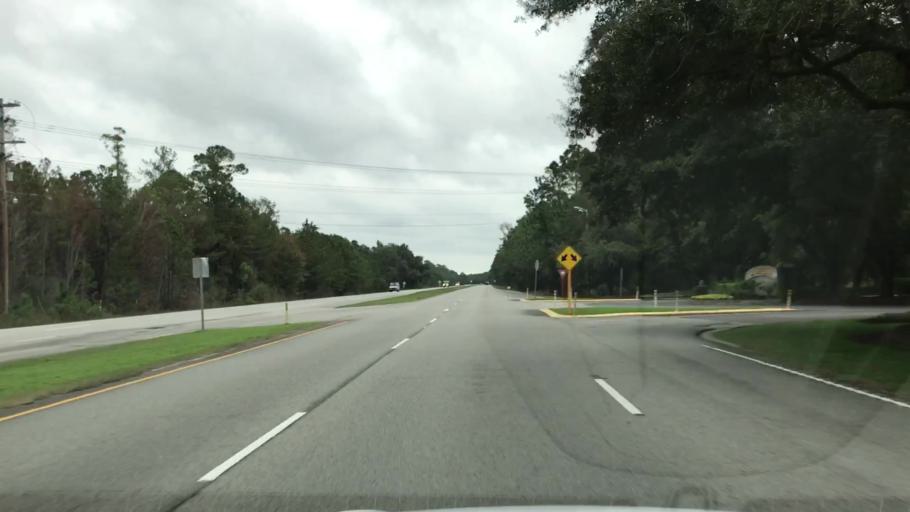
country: US
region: South Carolina
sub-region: Georgetown County
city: Georgetown
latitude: 33.3751
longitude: -79.2140
